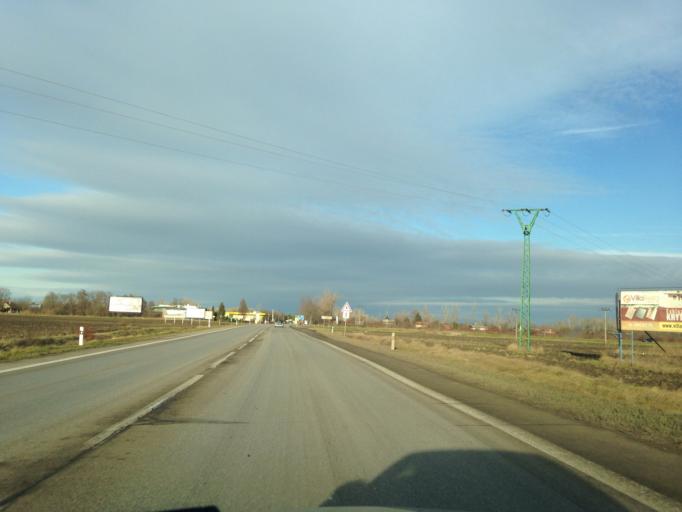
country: SK
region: Nitriansky
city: Komarno
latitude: 47.7648
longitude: 18.1522
